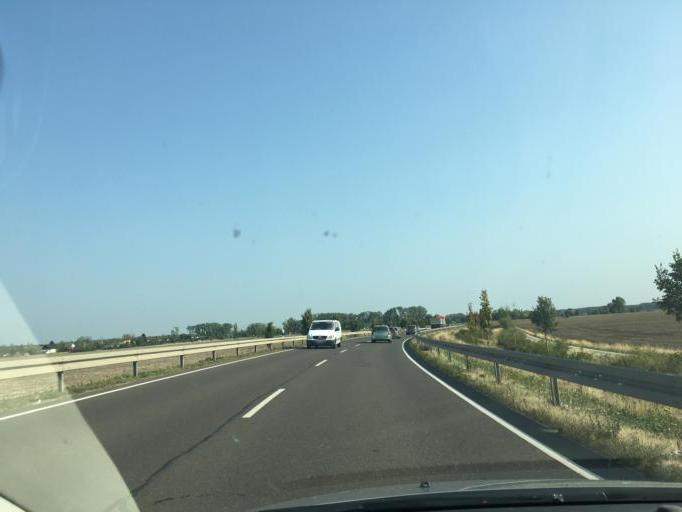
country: DE
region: Saxony-Anhalt
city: Schonebeck
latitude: 52.0072
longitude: 11.7723
